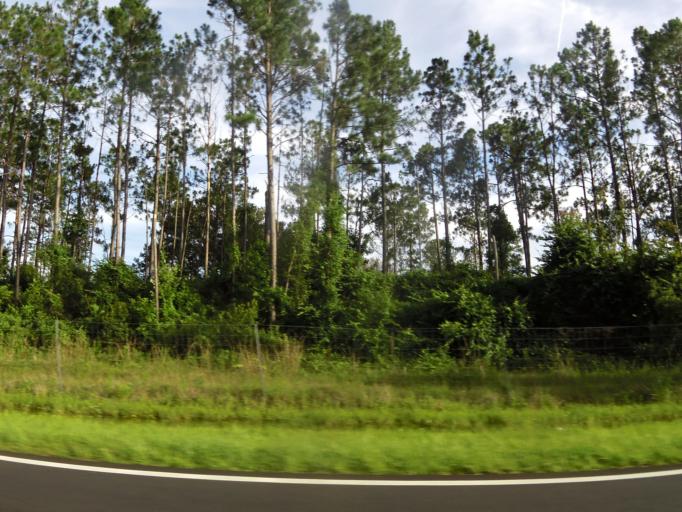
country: US
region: Florida
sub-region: Clay County
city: Green Cove Springs
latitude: 30.0144
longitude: -81.5968
